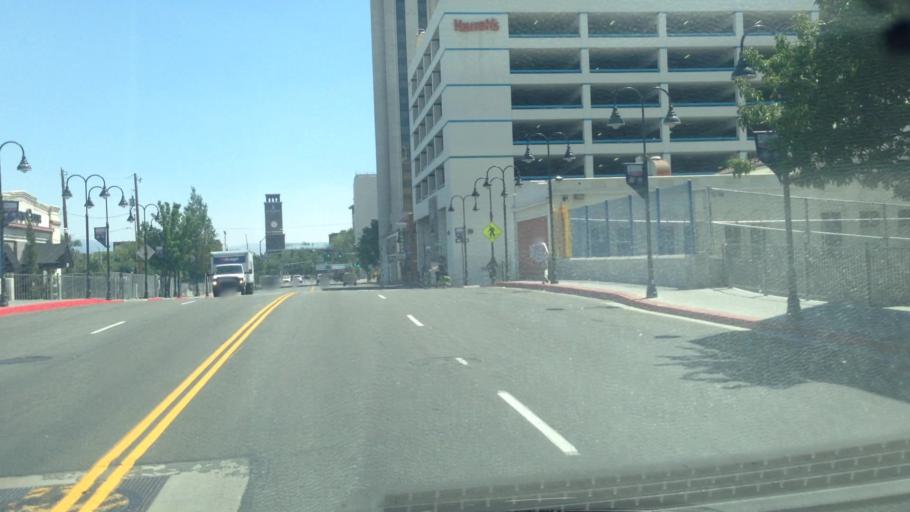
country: US
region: Nevada
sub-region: Washoe County
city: Reno
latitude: 39.5293
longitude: -119.8113
